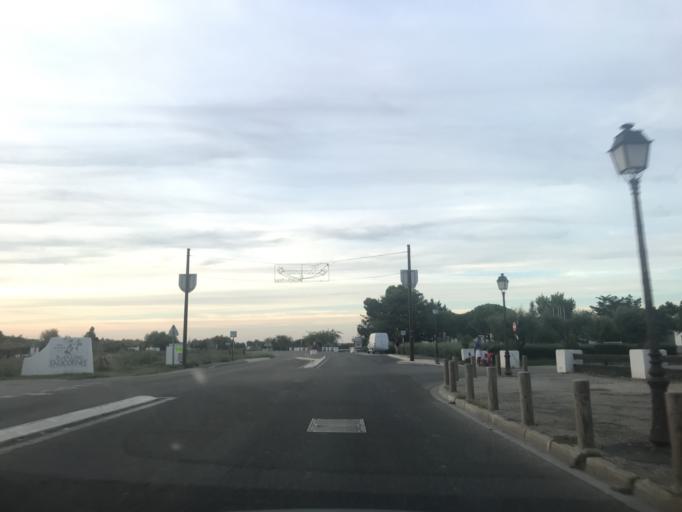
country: FR
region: Provence-Alpes-Cote d'Azur
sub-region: Departement des Bouches-du-Rhone
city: Saintes-Maries-de-la-Mer
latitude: 43.4564
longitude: 4.4270
